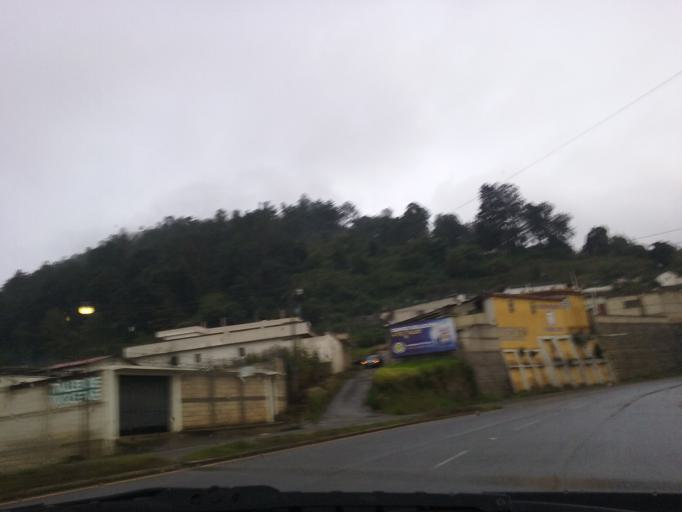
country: GT
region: Totonicapan
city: San Cristobal Totonicapan
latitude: 14.8996
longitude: -91.4385
